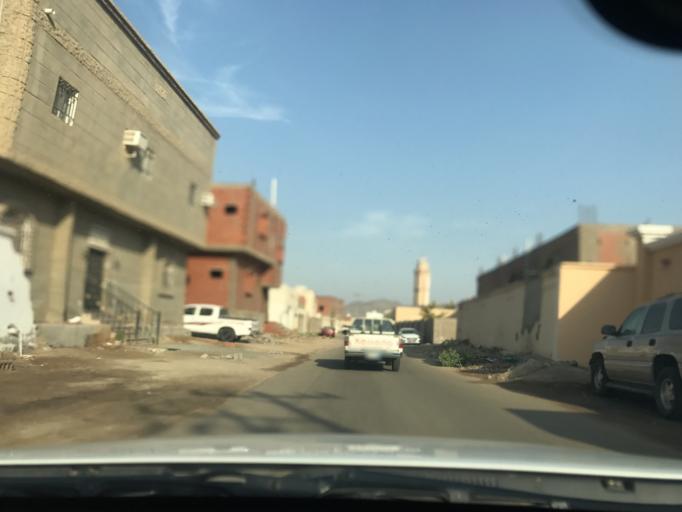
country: SA
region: Makkah
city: Al Jumum
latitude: 21.4410
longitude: 39.5213
